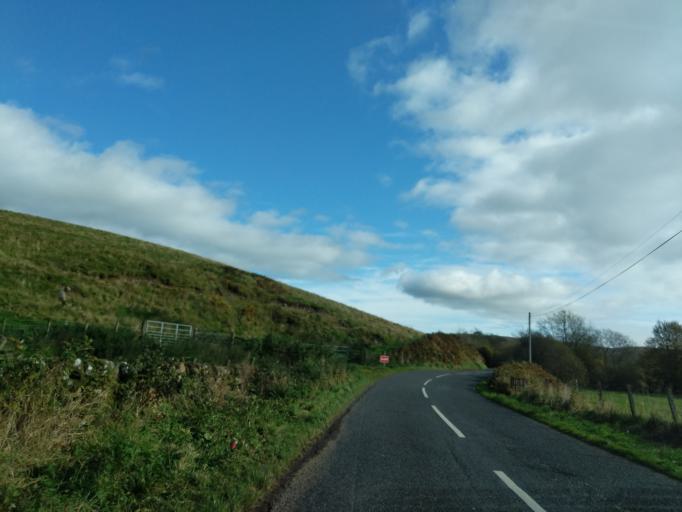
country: GB
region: Scotland
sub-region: Dumfries and Galloway
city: Sanquhar
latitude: 55.1618
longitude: -3.9817
